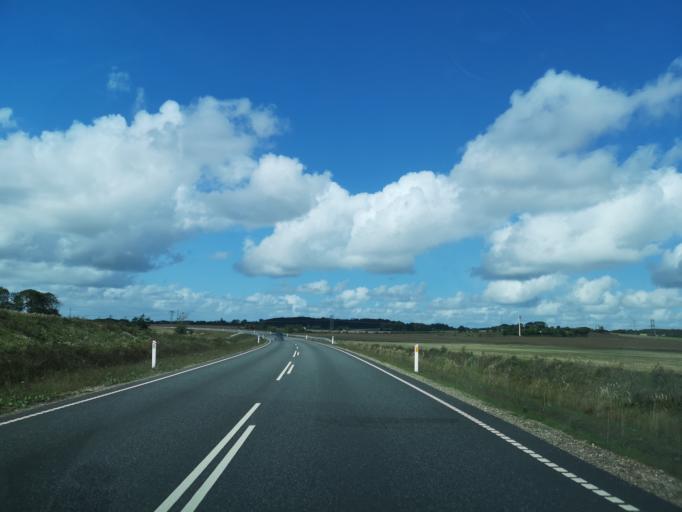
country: DK
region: Central Jutland
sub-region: Holstebro Kommune
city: Holstebro
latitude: 56.3950
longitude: 8.5772
